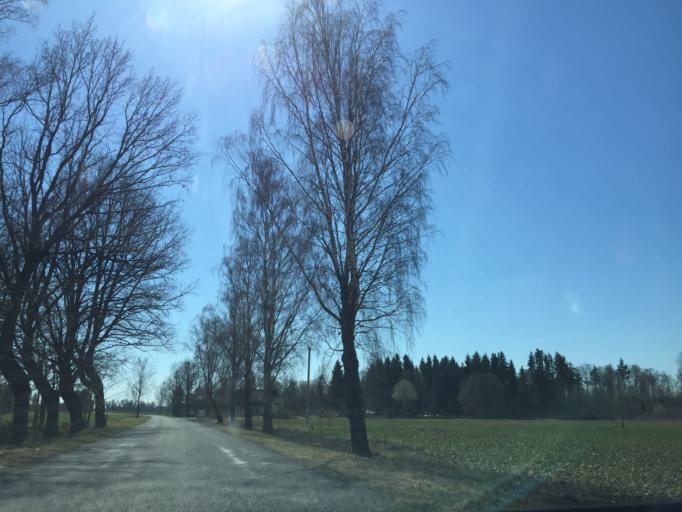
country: EE
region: Viljandimaa
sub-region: Viiratsi vald
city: Viiratsi
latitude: 58.3833
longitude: 25.7438
